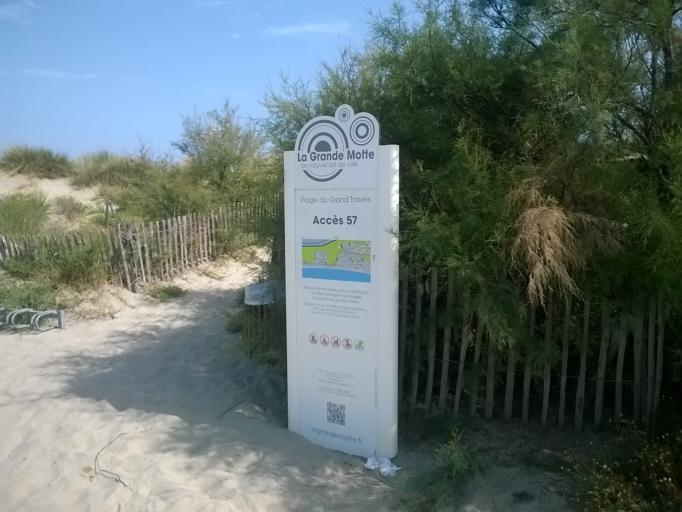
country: FR
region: Languedoc-Roussillon
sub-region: Departement de l'Herault
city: La Grande-Motte
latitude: 43.5575
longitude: 4.0420
